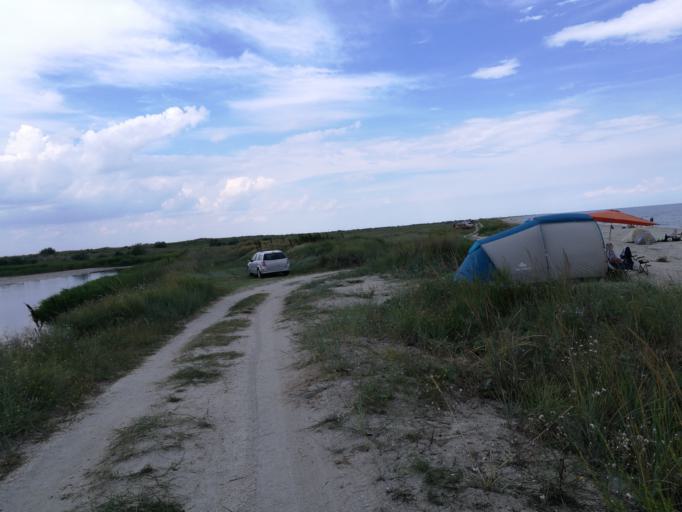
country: RO
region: Constanta
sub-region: Comuna Corbu
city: Corbu
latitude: 44.4303
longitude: 28.7692
